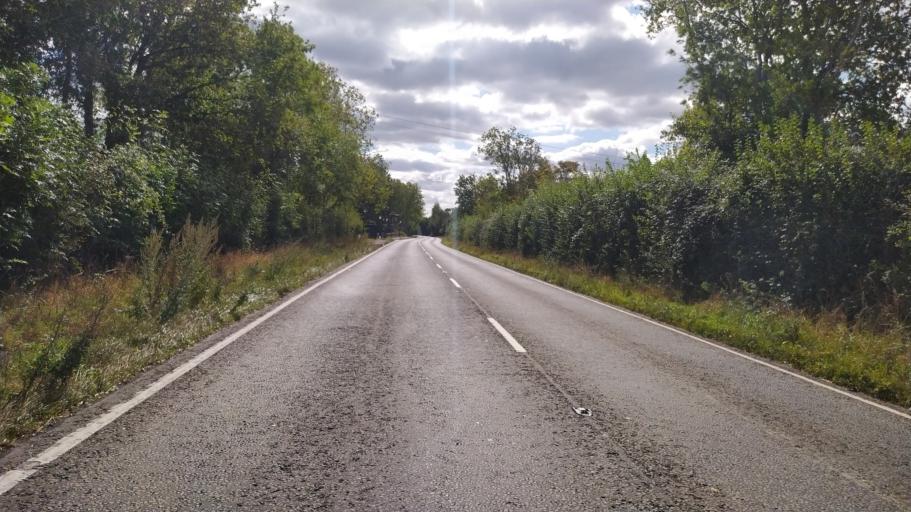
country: GB
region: England
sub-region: West Berkshire
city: Stratfield Mortimer
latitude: 51.3315
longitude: -1.0011
